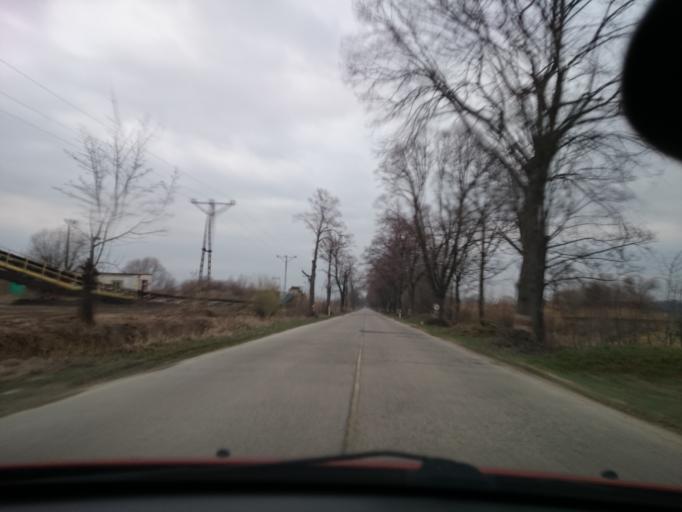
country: PL
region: Opole Voivodeship
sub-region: Powiat nyski
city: Kamienica
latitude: 50.4944
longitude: 16.9617
